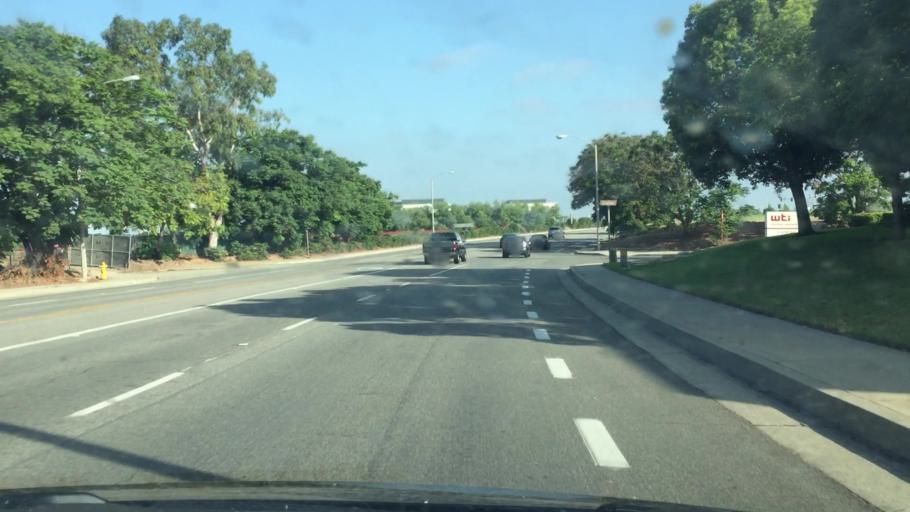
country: US
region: California
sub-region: Orange County
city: Lake Forest
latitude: 33.6455
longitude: -117.7234
